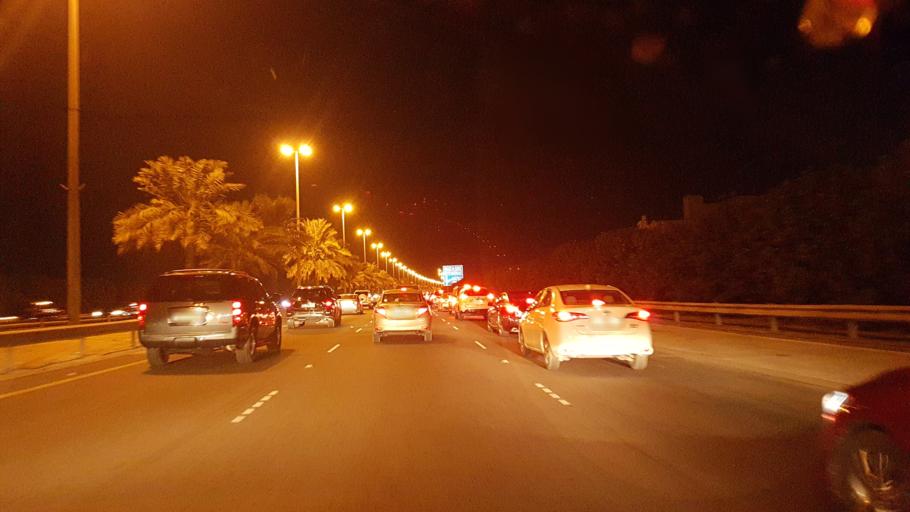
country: BH
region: Central Governorate
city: Madinat Hamad
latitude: 26.1557
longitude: 50.5065
